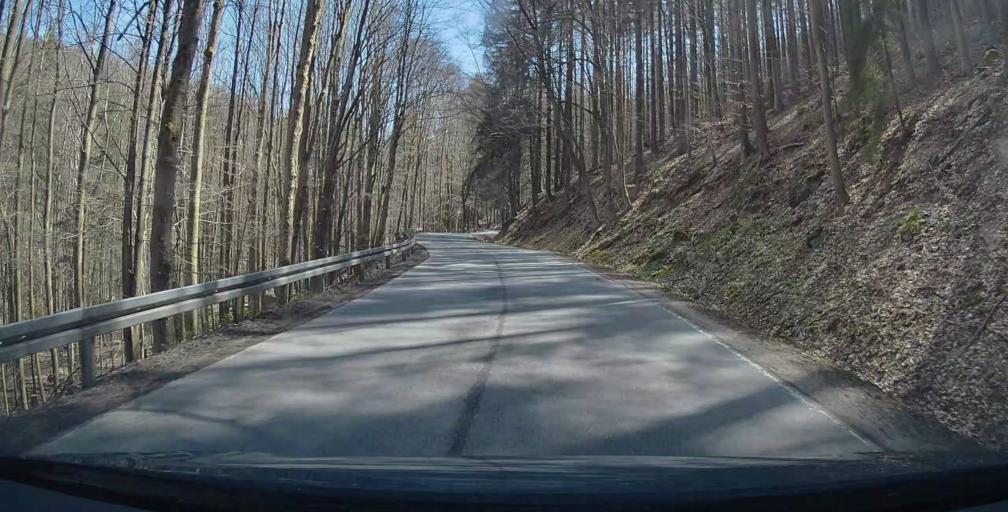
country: PL
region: Lower Silesian Voivodeship
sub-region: Powiat klodzki
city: Kudowa-Zdroj
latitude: 50.4507
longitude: 16.2848
